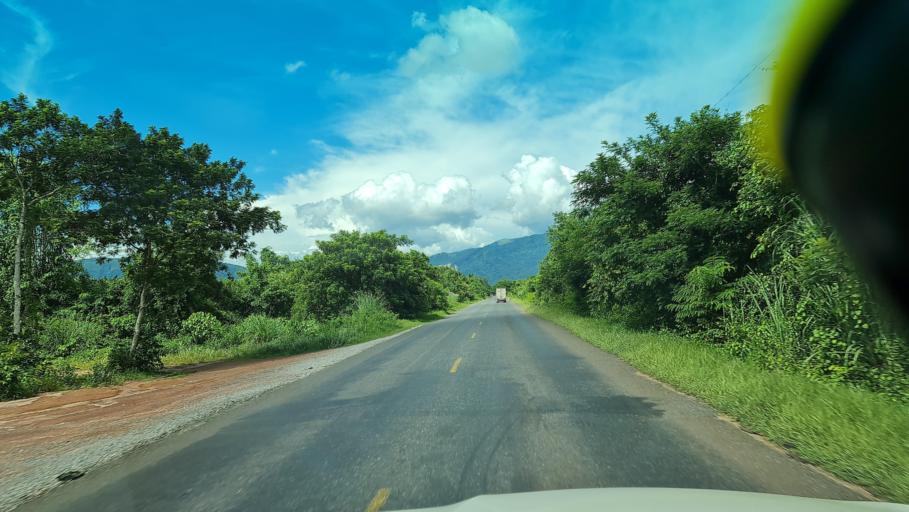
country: LA
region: Bolikhamxai
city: Pakkading
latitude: 18.2946
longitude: 104.0865
